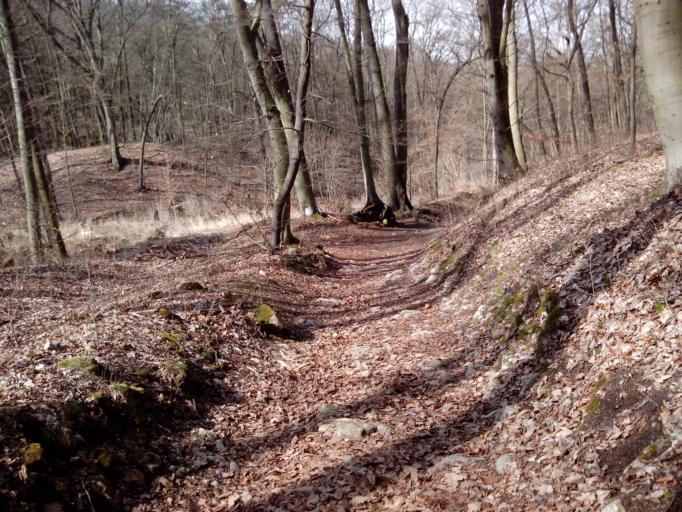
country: CZ
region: Central Bohemia
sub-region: Okres Beroun
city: Beroun
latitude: 49.9408
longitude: 14.1045
